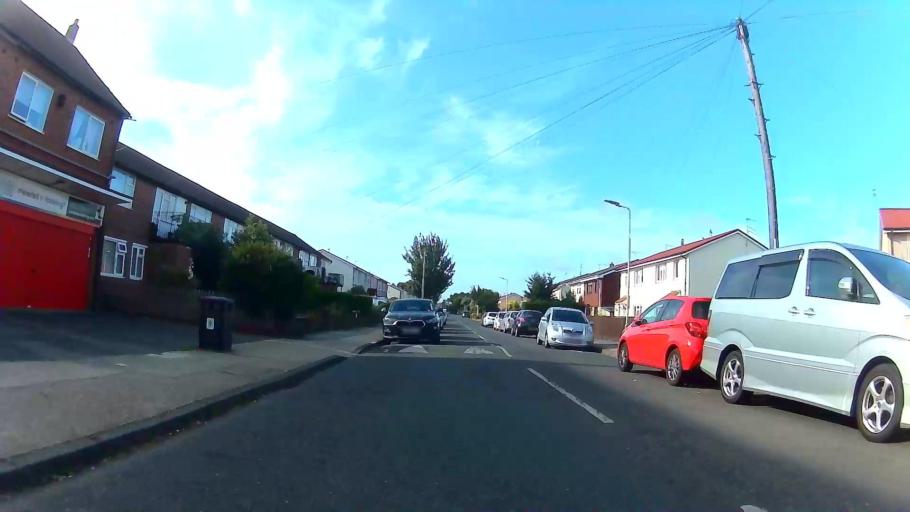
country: GB
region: England
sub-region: Greater London
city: Elm Park
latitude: 51.5595
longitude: 0.1959
